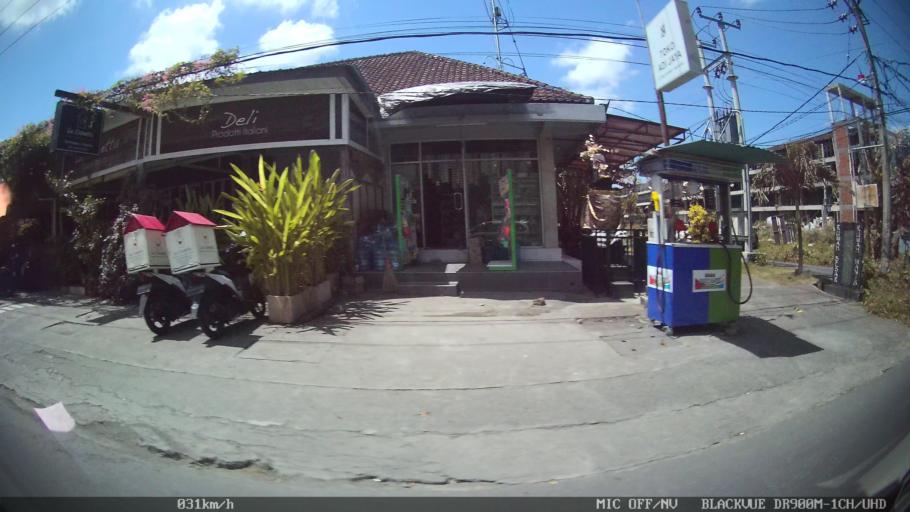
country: ID
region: Bali
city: Banjar Gunungpande
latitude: -8.6616
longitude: 115.1525
